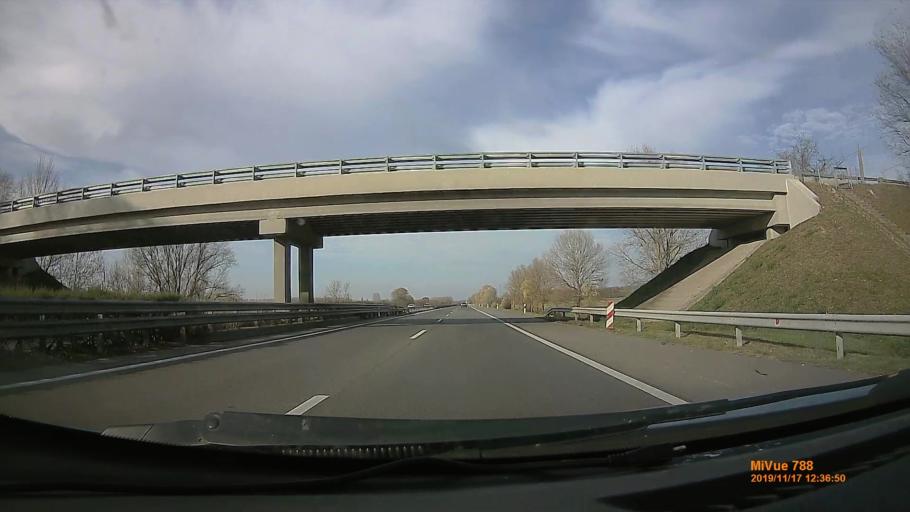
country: HU
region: Pest
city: Taborfalva
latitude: 47.0953
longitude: 19.5180
